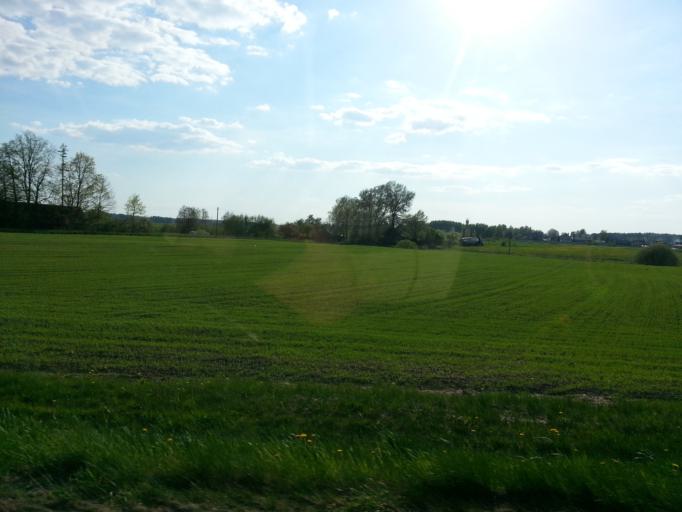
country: LT
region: Panevezys
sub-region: Panevezys City
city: Panevezys
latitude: 55.8428
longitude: 24.3563
